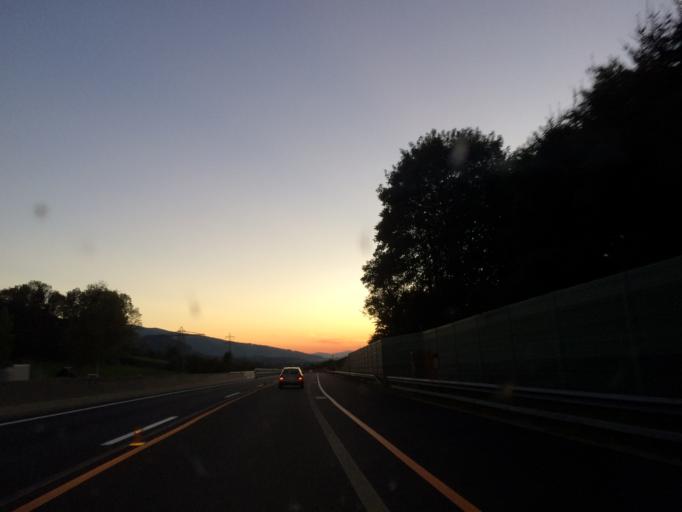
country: AT
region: Styria
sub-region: Politischer Bezirk Bruck-Muerzzuschlag
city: Langenwang
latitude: 47.5774
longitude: 15.6523
